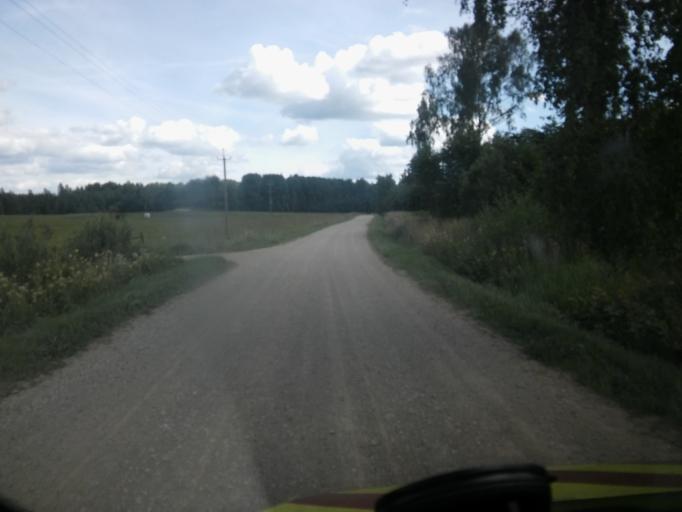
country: EE
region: Viljandimaa
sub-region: Karksi vald
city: Karksi-Nuia
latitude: 58.0821
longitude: 25.5141
